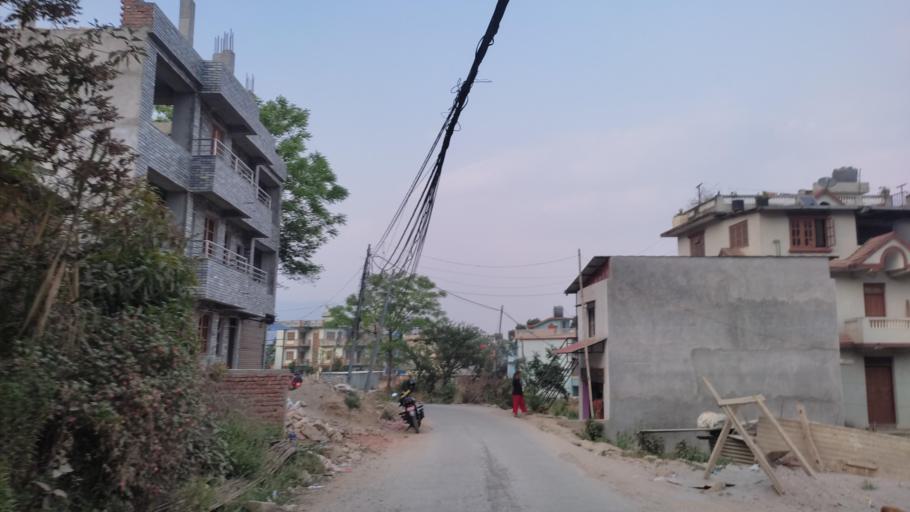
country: NP
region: Central Region
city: Kirtipur
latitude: 27.6750
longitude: 85.2458
